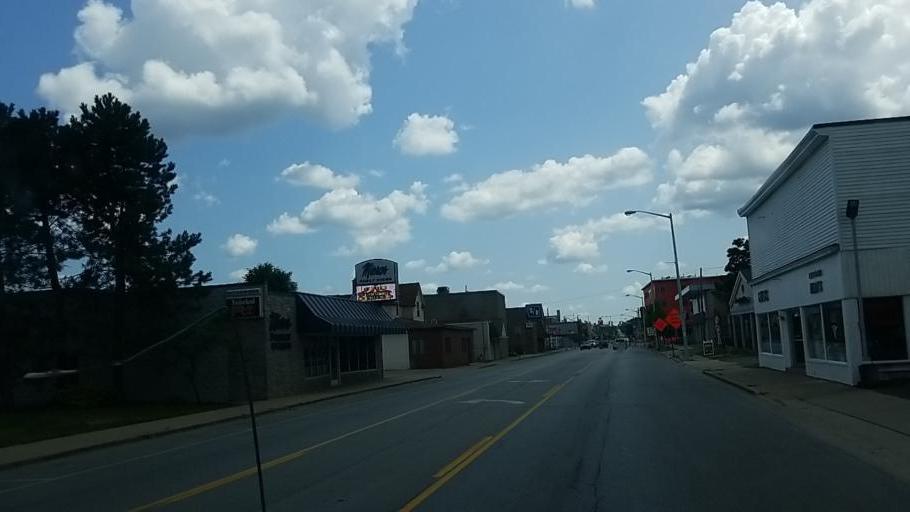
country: US
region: Michigan
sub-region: Kent County
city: Grand Rapids
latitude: 42.9852
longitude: -85.6902
